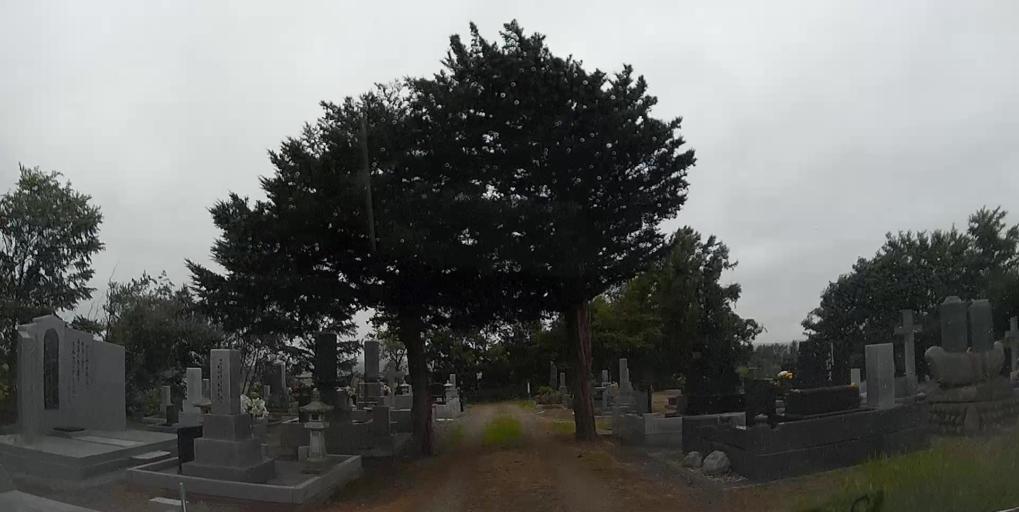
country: JP
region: Hokkaido
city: Iwanai
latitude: 42.4319
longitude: 139.9711
